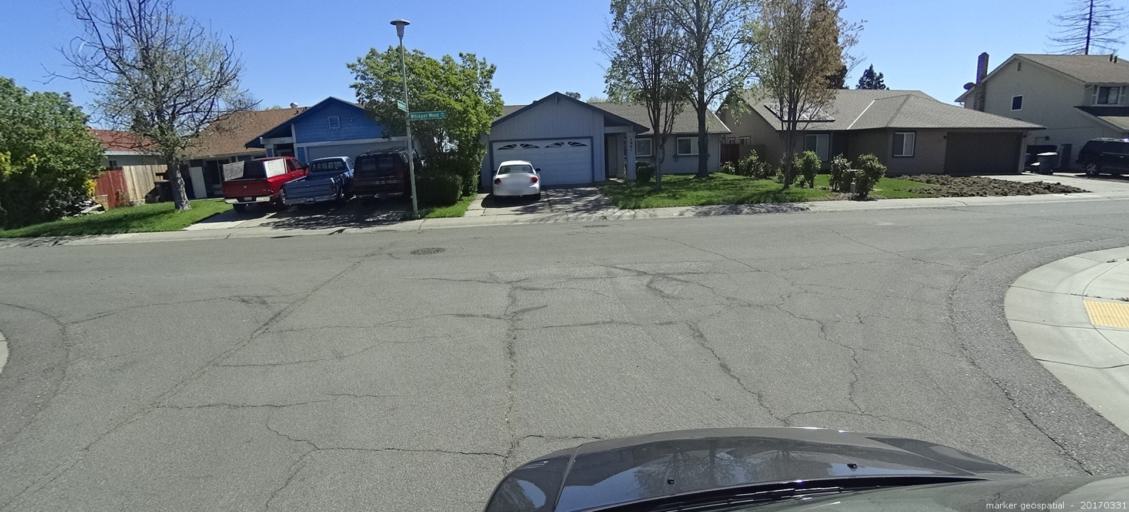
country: US
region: California
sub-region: Sacramento County
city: Parkway
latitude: 38.4695
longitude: -121.4472
